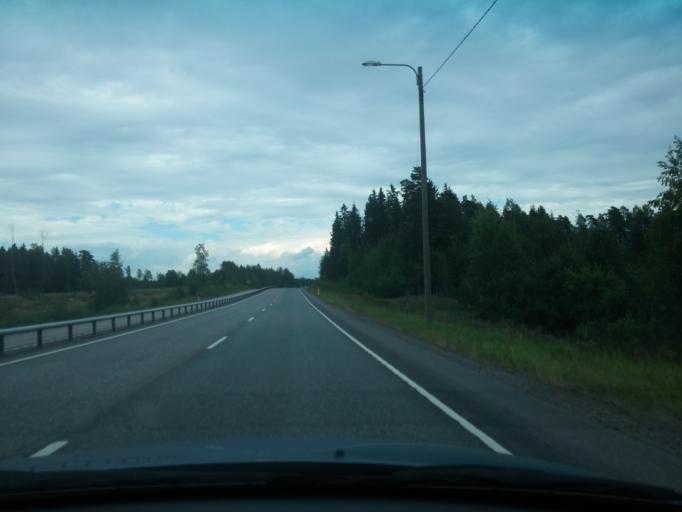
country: FI
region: Haeme
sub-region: Riihimaeki
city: Loppi
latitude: 60.7190
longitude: 24.4947
